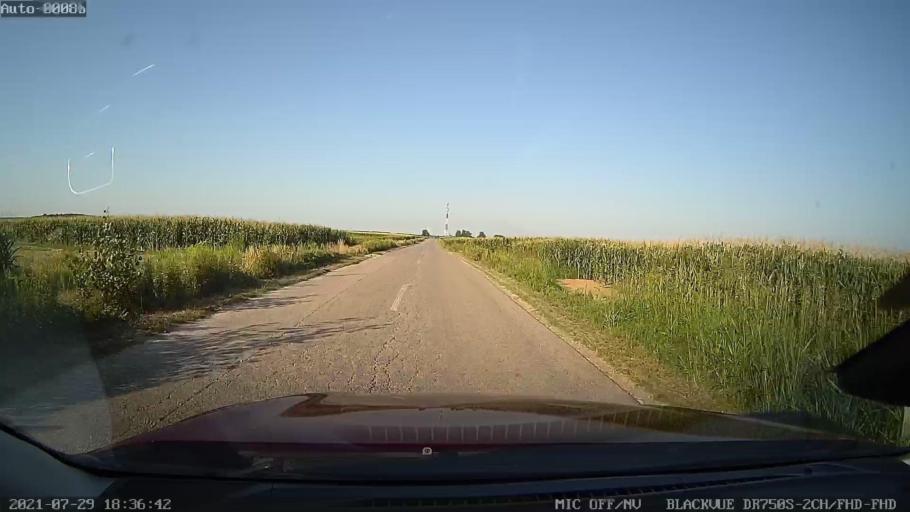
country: HR
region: Varazdinska
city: Vinica
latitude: 46.3180
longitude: 16.1887
